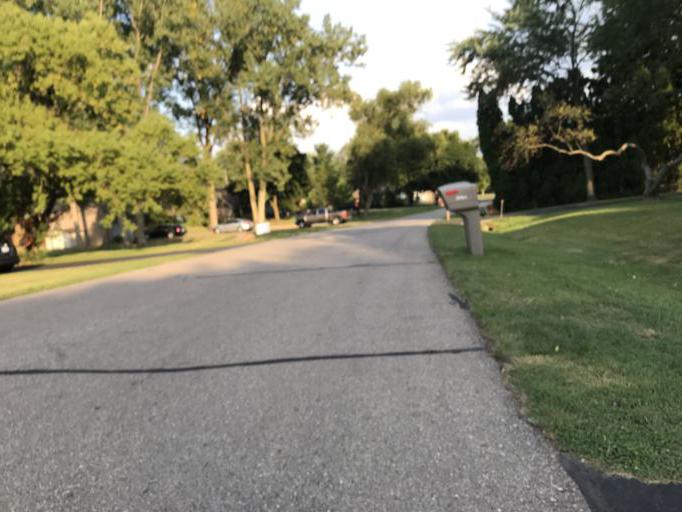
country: US
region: Michigan
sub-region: Oakland County
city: Farmington Hills
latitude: 42.4890
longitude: -83.3559
